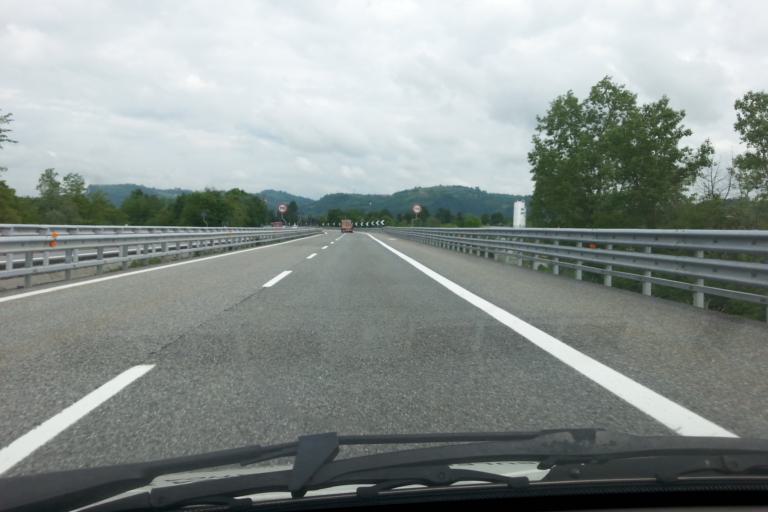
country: IT
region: Piedmont
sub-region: Provincia di Cuneo
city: Lesegno
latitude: 44.4073
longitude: 7.9695
